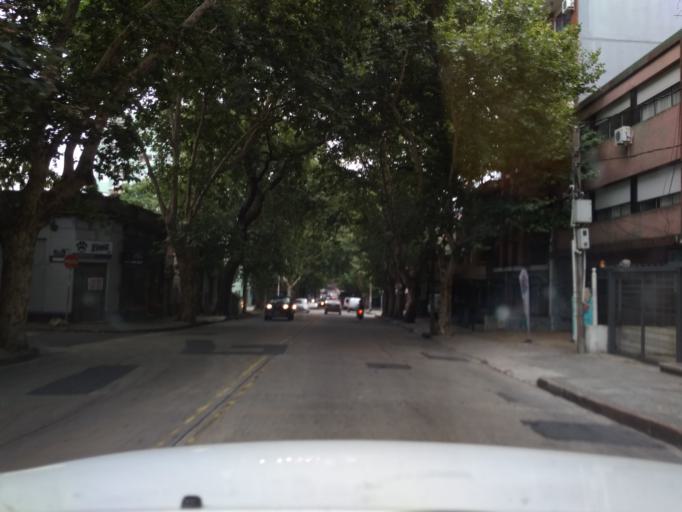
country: UY
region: Montevideo
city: Montevideo
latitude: -34.9029
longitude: -56.1468
